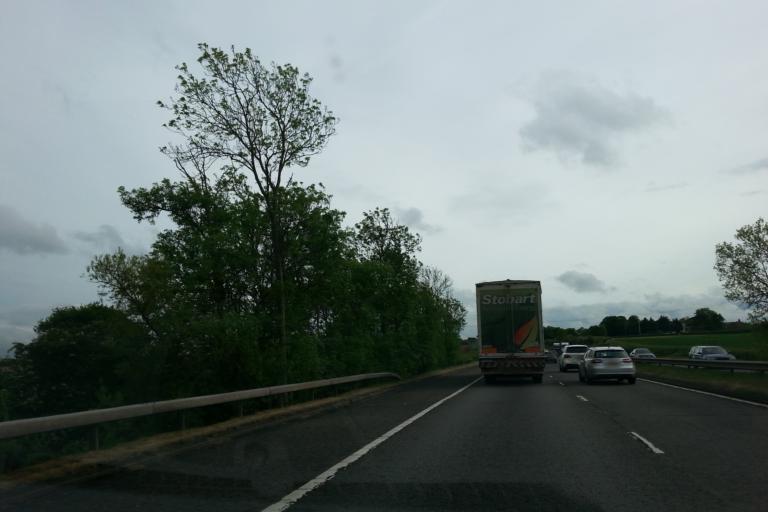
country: GB
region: England
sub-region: Nottinghamshire
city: Bircotes
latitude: 53.3740
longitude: -1.0539
